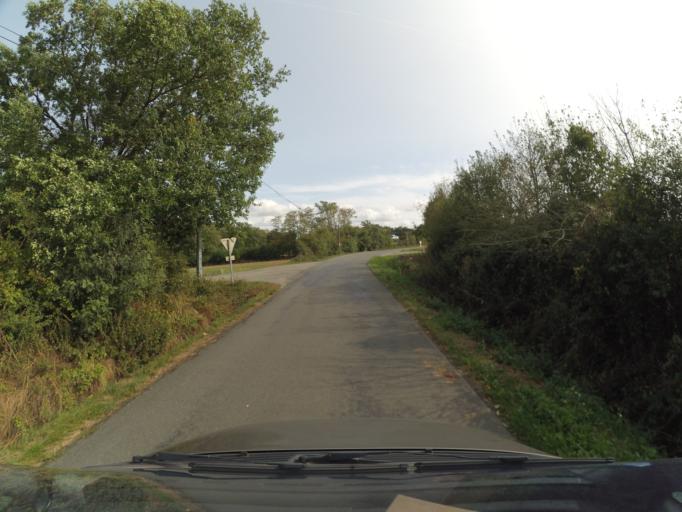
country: FR
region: Pays de la Loire
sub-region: Departement de la Vendee
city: La Bruffiere
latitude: 47.0030
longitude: -1.2007
